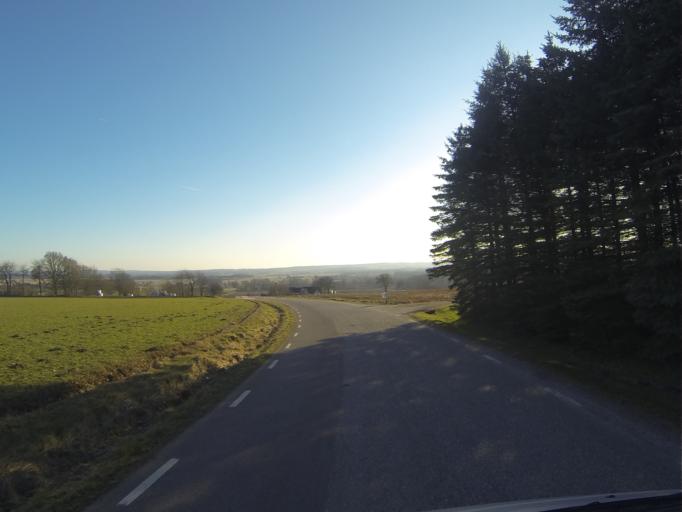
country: SE
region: Skane
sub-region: Hoors Kommun
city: Loberod
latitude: 55.7470
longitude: 13.4424
